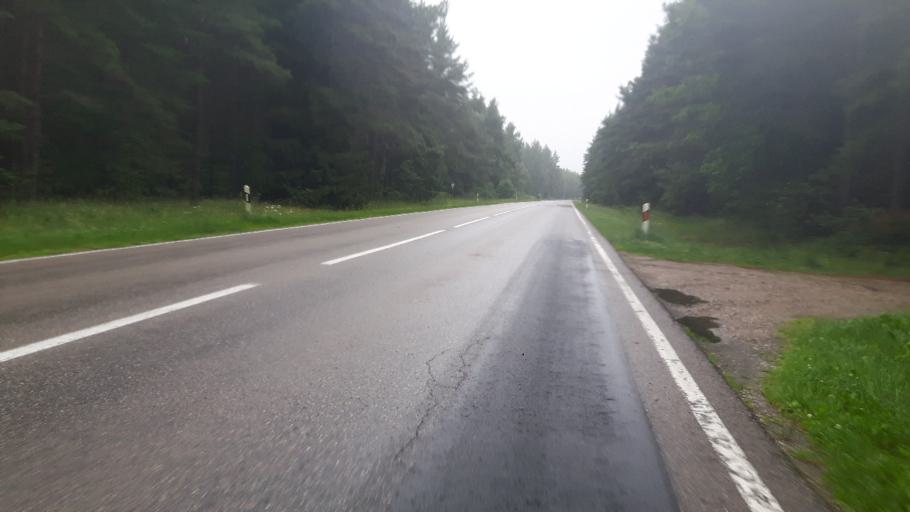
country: LT
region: Klaipedos apskritis
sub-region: Palanga
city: Sventoji
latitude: 56.0628
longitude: 21.1203
